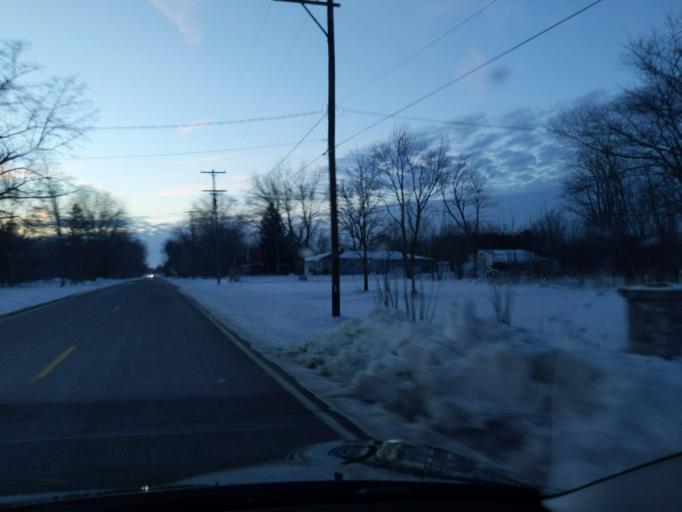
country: US
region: Michigan
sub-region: Ingham County
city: Mason
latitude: 42.5822
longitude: -84.4184
